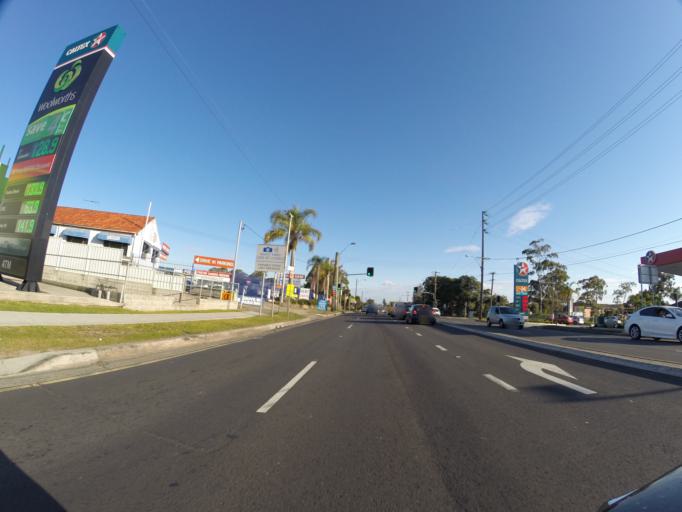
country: AU
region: New South Wales
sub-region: Fairfield
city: Fairfield East
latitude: -33.8668
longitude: 150.9884
